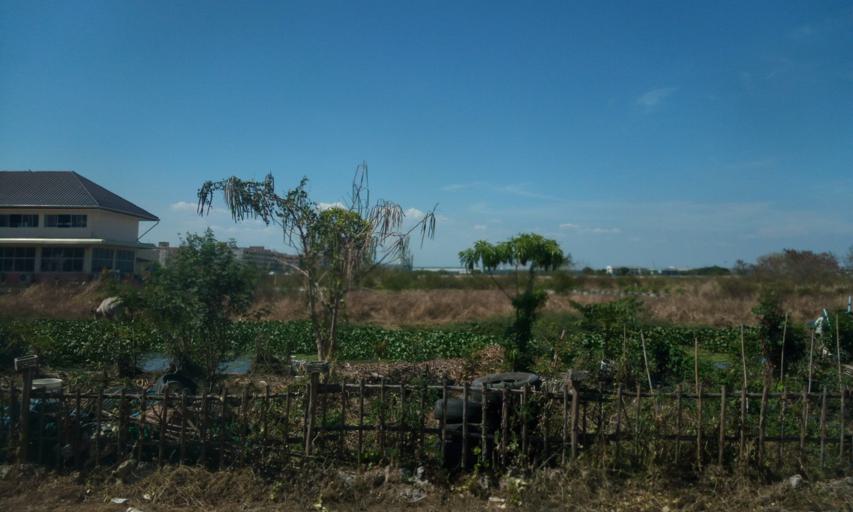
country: TH
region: Samut Prakan
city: Bang Bo District
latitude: 13.5569
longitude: 100.7676
